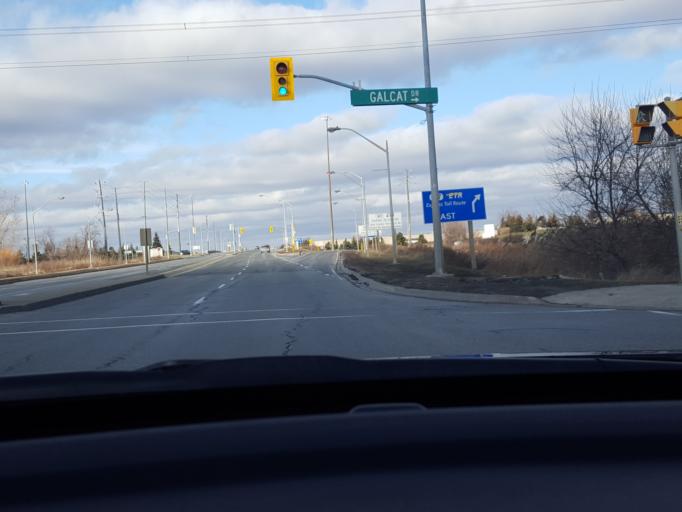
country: CA
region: Ontario
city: Concord
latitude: 43.7704
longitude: -79.5695
